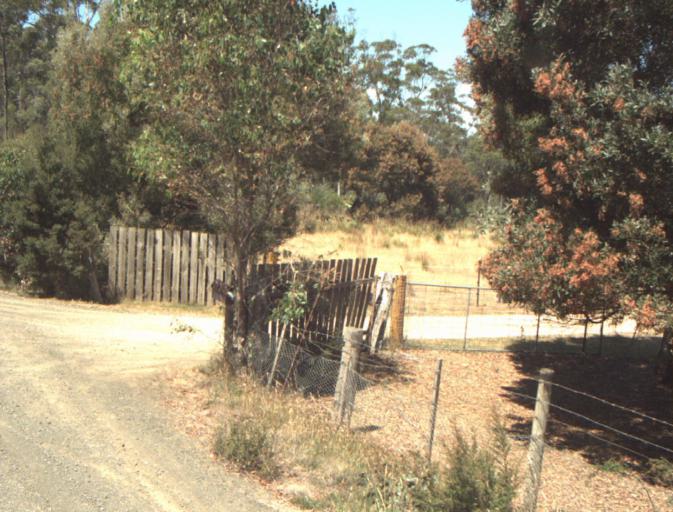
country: AU
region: Tasmania
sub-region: Launceston
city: Mayfield
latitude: -41.2718
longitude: 147.0990
